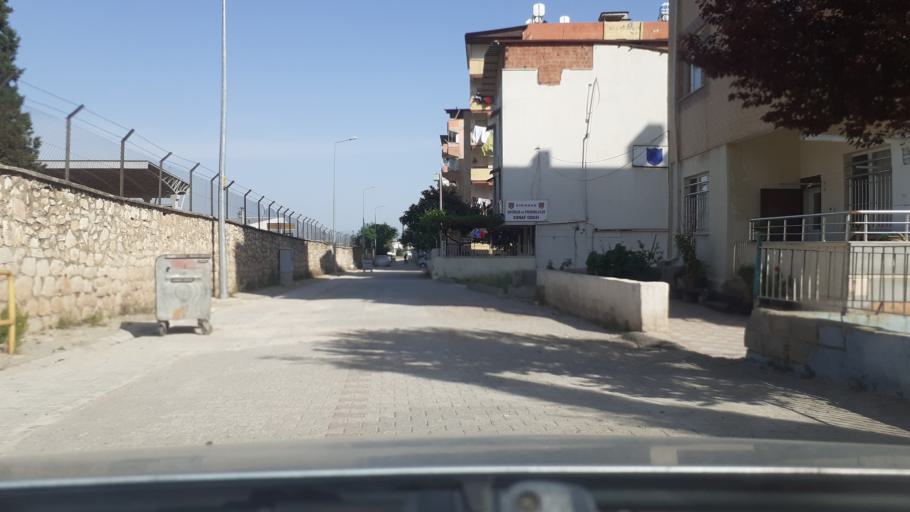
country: TR
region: Hatay
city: Kirikhan
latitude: 36.4924
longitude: 36.3673
